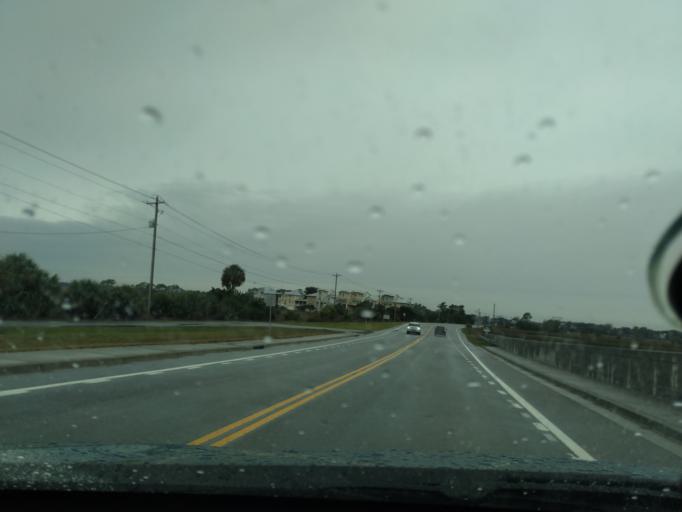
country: US
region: South Carolina
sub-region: Charleston County
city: Folly Beach
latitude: 32.6765
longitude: -79.9519
